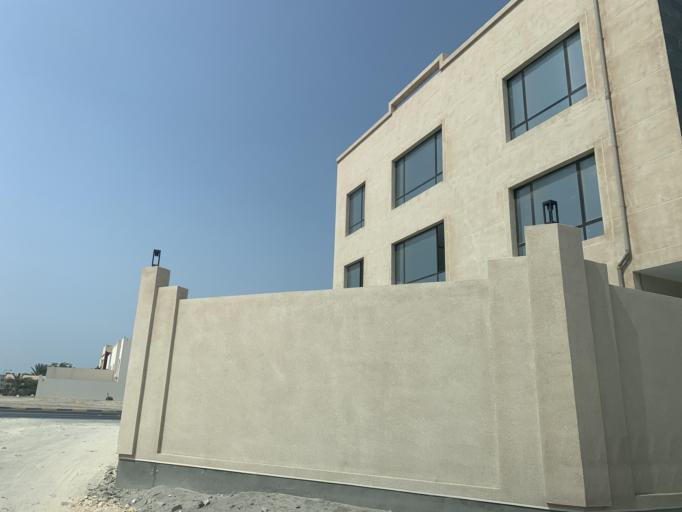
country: BH
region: Muharraq
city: Al Hadd
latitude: 26.2670
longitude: 50.6572
